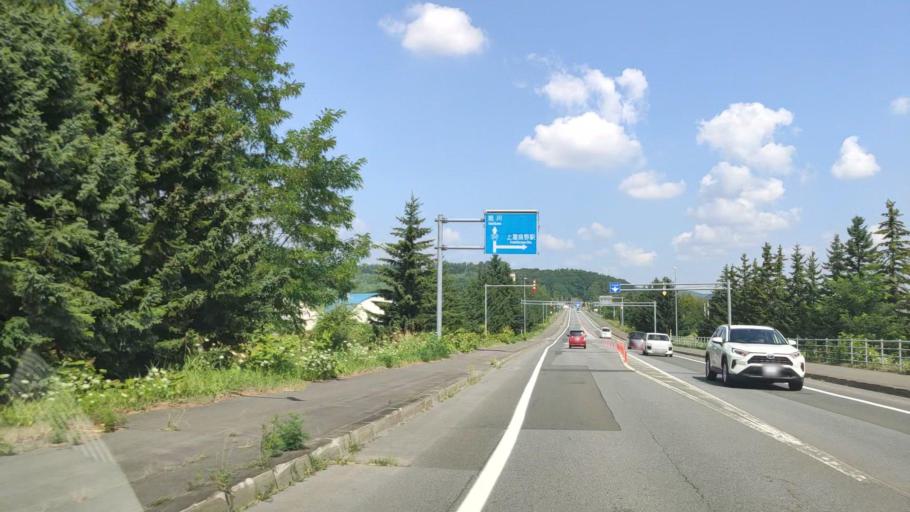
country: JP
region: Hokkaido
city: Shimo-furano
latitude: 43.4647
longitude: 142.4562
